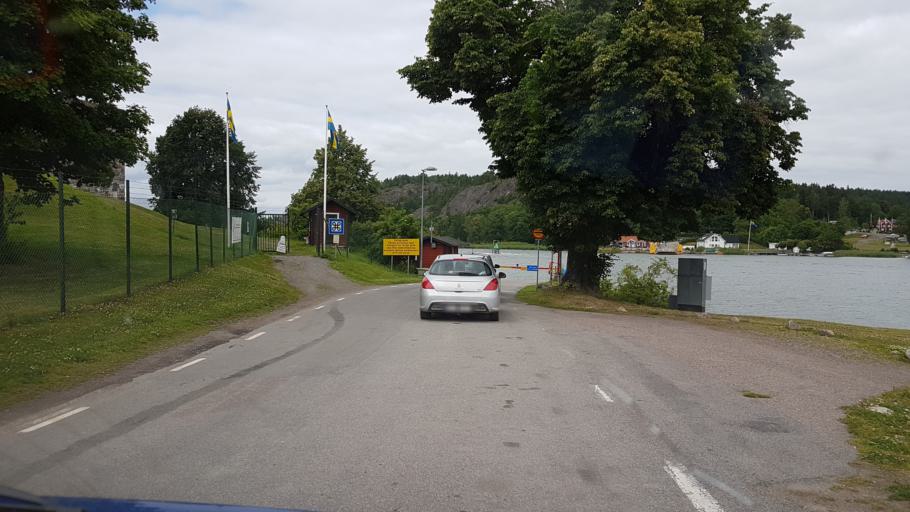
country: SE
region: OEstergoetland
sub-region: Valdemarsviks Kommun
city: Gusum
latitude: 58.4416
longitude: 16.5999
